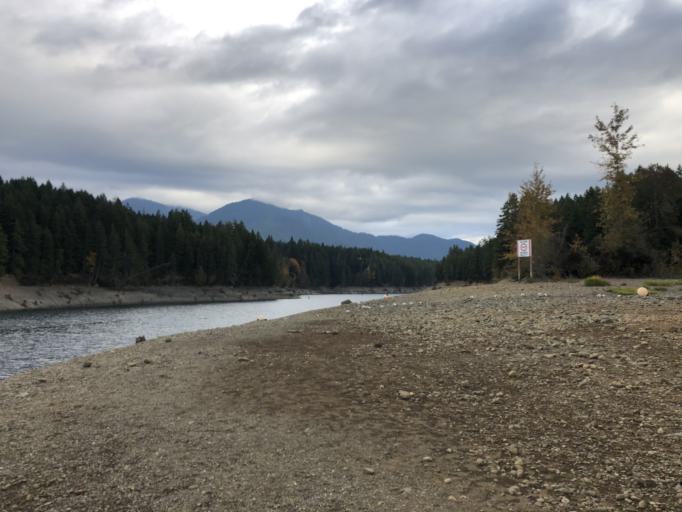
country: US
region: Washington
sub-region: Mason County
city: Shelton
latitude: 47.4637
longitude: -123.2231
